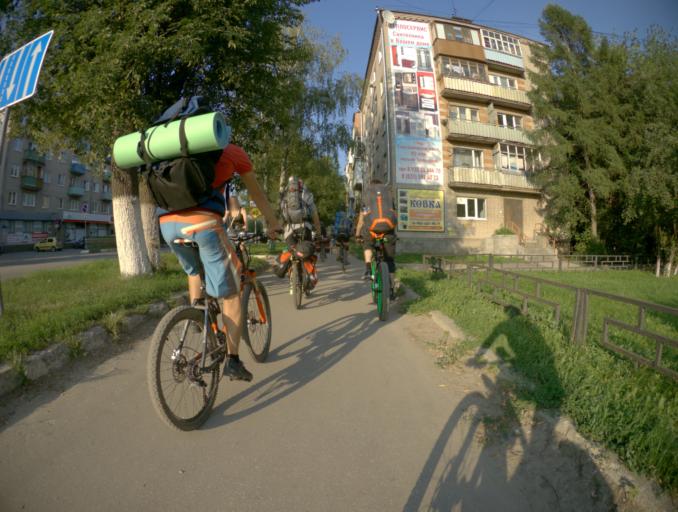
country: RU
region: Nizjnij Novgorod
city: Bor
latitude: 56.3625
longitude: 44.0628
